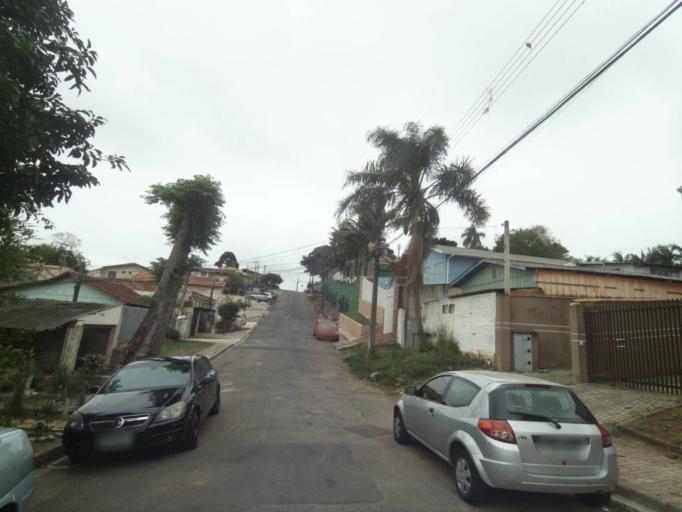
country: BR
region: Parana
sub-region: Sao Jose Dos Pinhais
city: Sao Jose dos Pinhais
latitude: -25.4848
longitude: -49.2314
